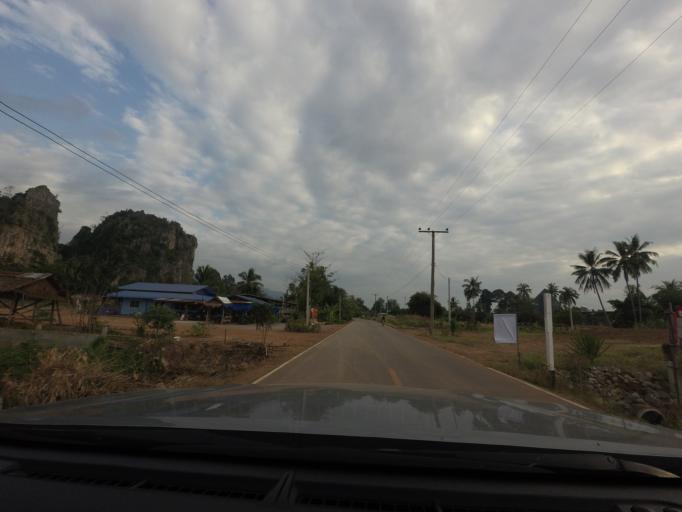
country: TH
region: Phitsanulok
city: Noen Maprang
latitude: 16.5656
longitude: 100.6904
